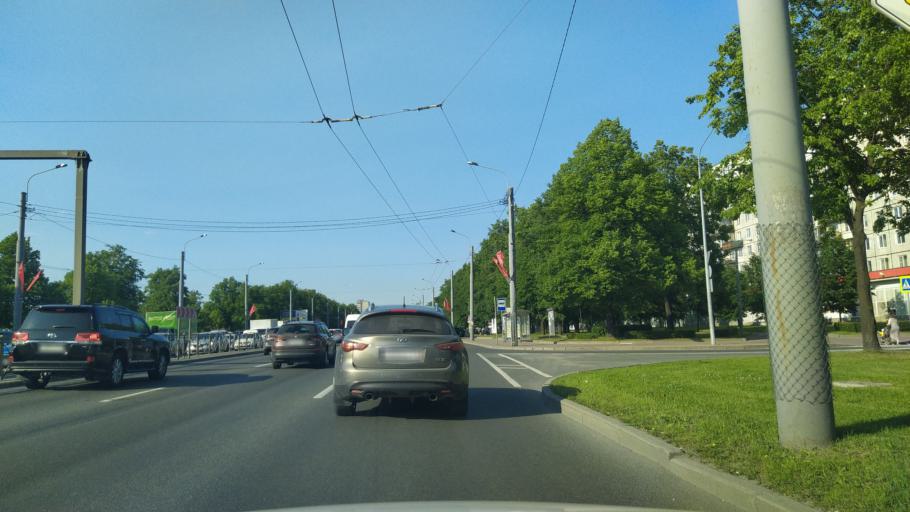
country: RU
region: Leningrad
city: Kalininskiy
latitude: 59.9760
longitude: 30.4170
